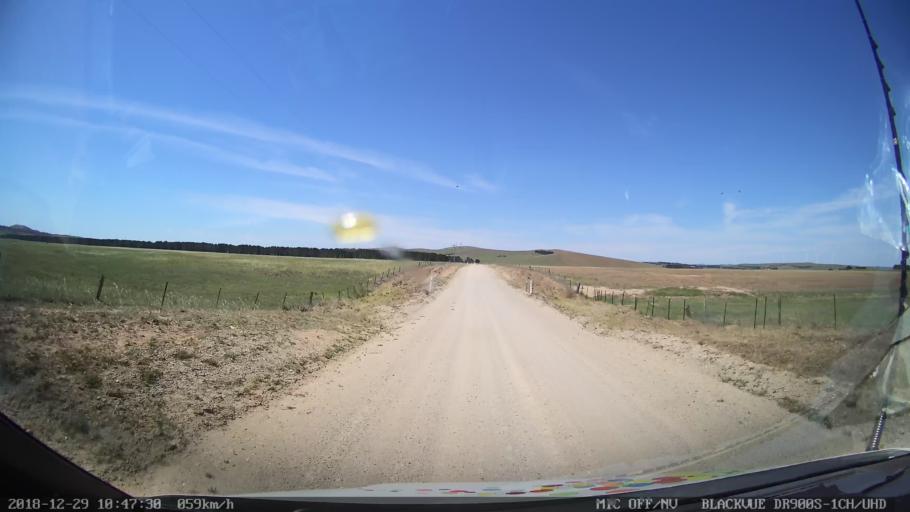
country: AU
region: New South Wales
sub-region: Palerang
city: Bungendore
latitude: -35.0598
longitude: 149.5159
